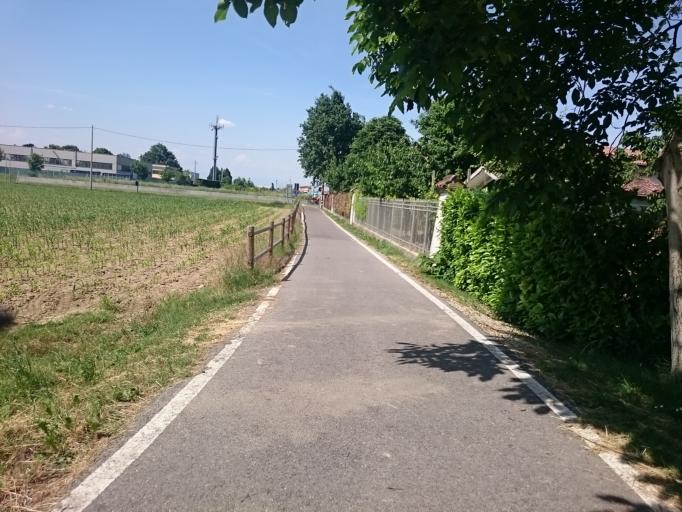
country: IT
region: Veneto
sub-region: Provincia di Padova
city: Bastia
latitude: 45.3807
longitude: 11.6469
